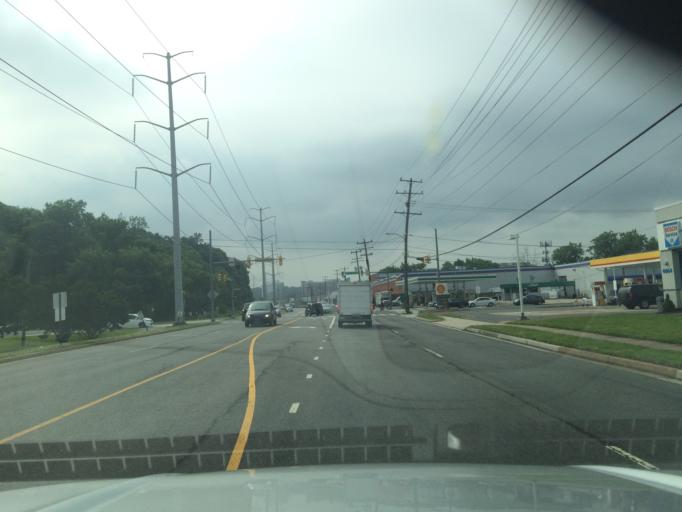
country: US
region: Virginia
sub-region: Fairfax County
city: Baileys Crossroads
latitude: 38.8473
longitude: -77.0961
